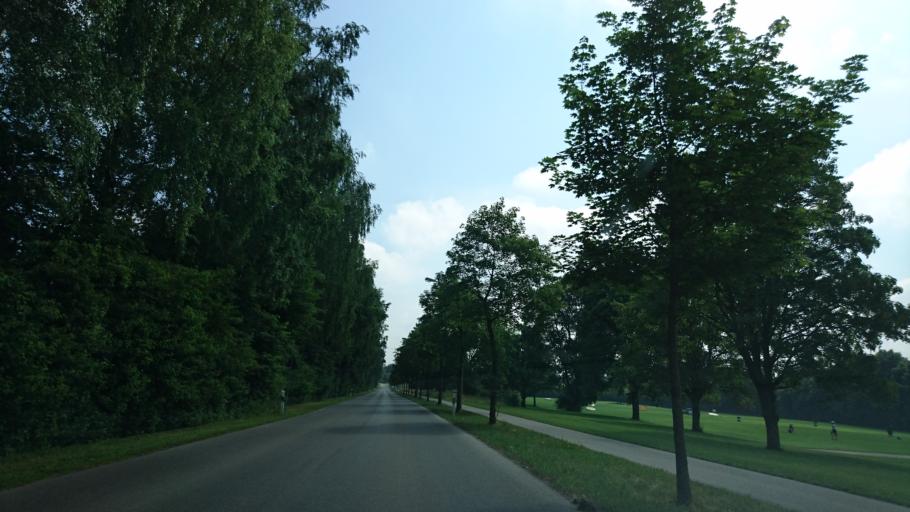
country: DE
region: Bavaria
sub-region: Swabia
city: Stadtbergen
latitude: 48.3641
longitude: 10.8296
